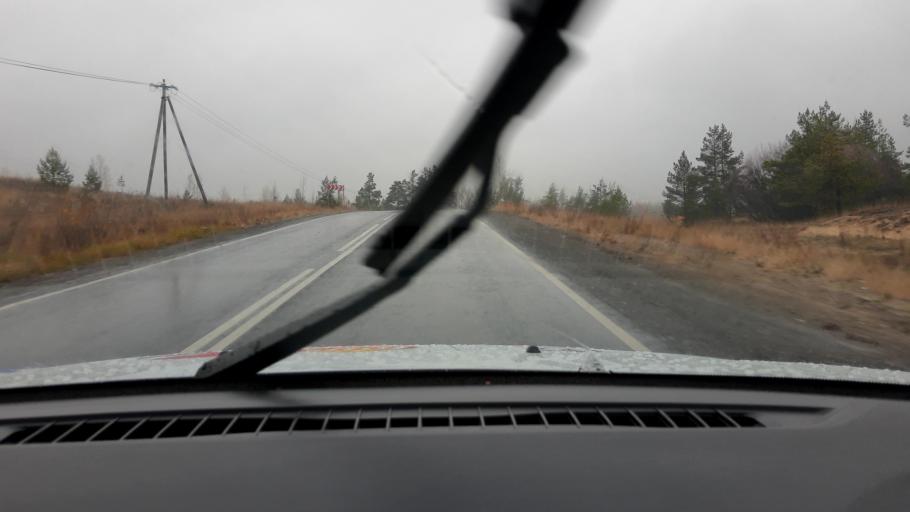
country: RU
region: Nizjnij Novgorod
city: Babino
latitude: 56.2738
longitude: 43.5921
